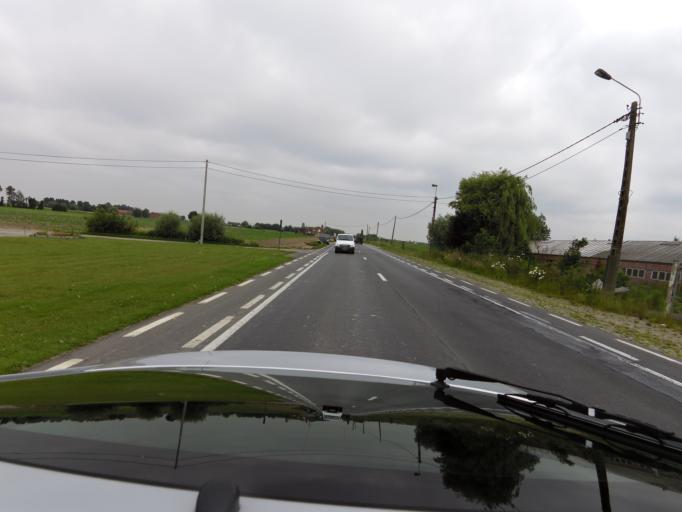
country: BE
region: Flanders
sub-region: Provincie West-Vlaanderen
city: Alveringem
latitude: 51.0155
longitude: 2.6812
